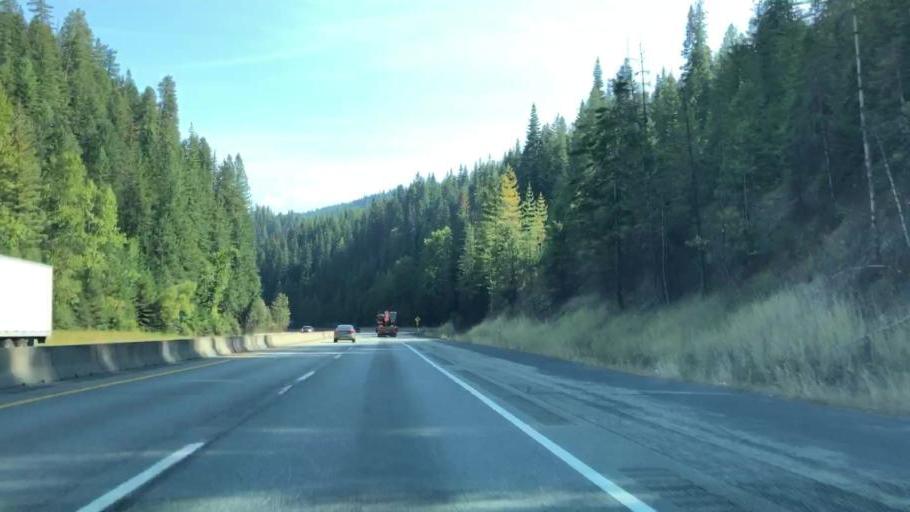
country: US
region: Idaho
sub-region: Shoshone County
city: Pinehurst
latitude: 47.6015
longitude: -116.4981
